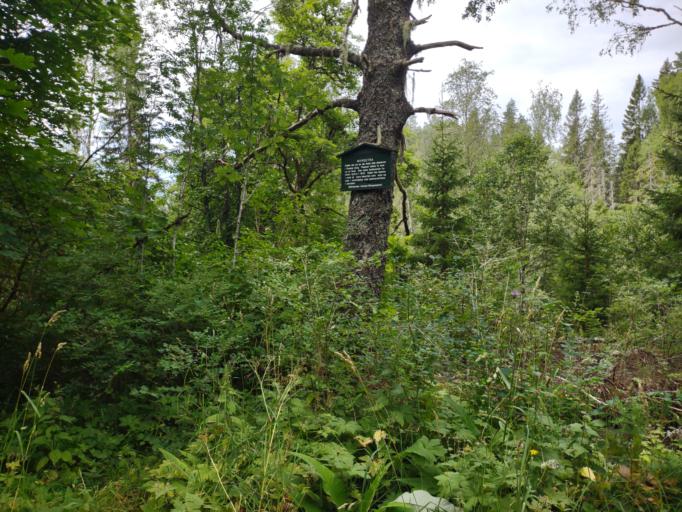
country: NO
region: Akershus
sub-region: Enebakk
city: Flateby
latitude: 59.8120
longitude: 11.0624
